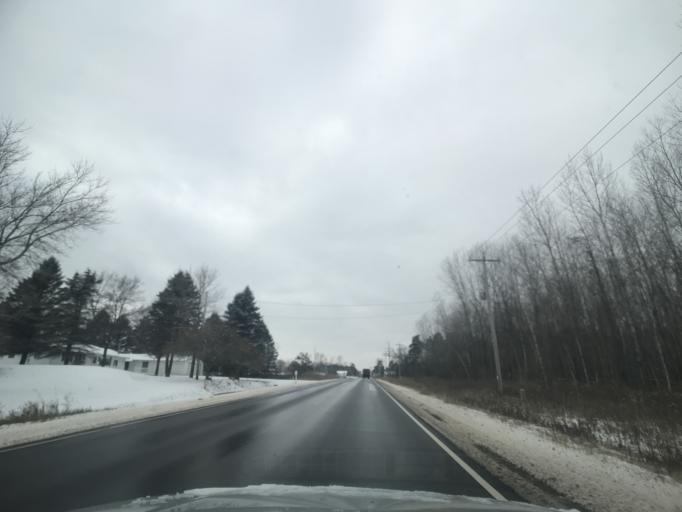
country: US
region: Wisconsin
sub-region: Brown County
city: Suamico
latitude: 44.7210
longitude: -88.0613
